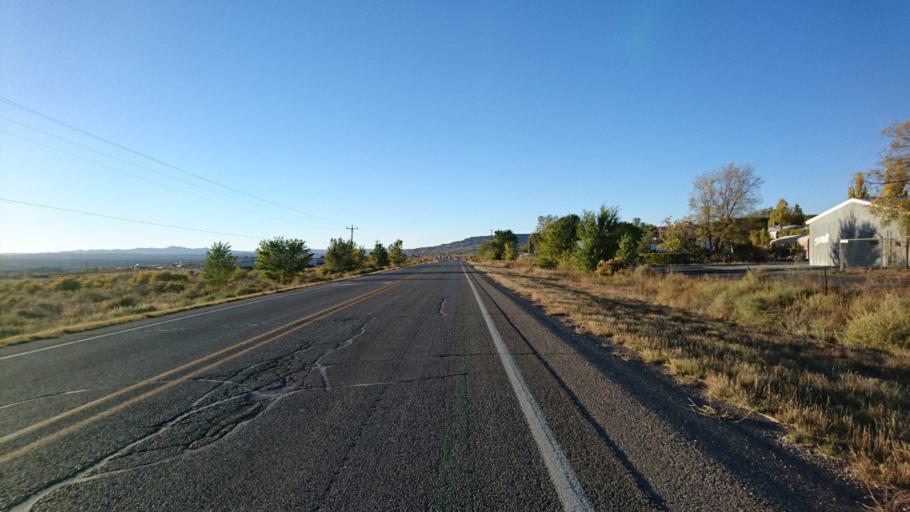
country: US
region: New Mexico
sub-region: Cibola County
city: Grants
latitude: 35.1284
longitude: -107.8070
